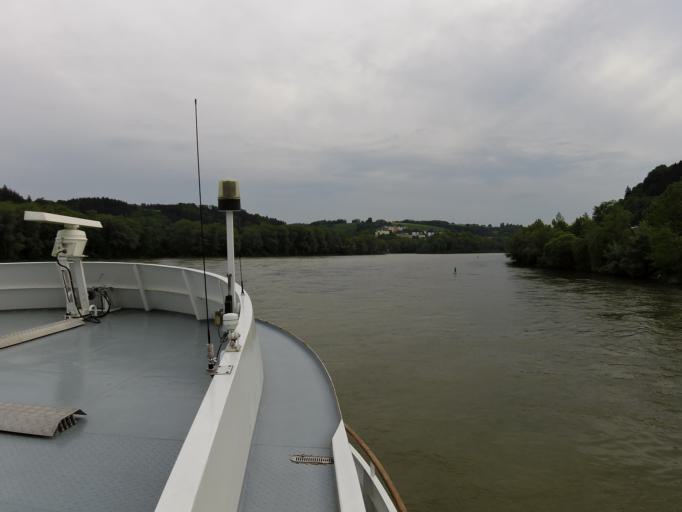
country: DE
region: Bavaria
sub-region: Lower Bavaria
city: Salzweg
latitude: 48.5797
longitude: 13.4995
